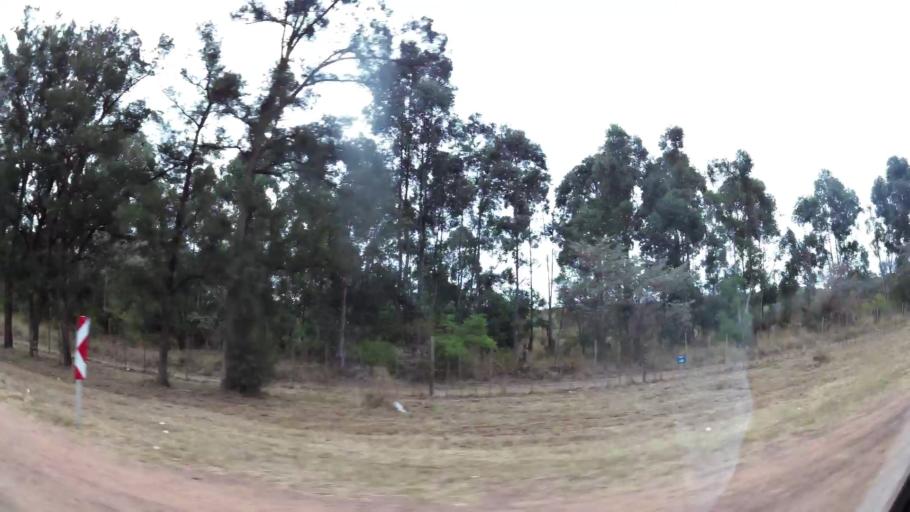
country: ZA
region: Limpopo
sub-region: Waterberg District Municipality
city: Modimolle
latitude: -24.6760
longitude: 28.4426
